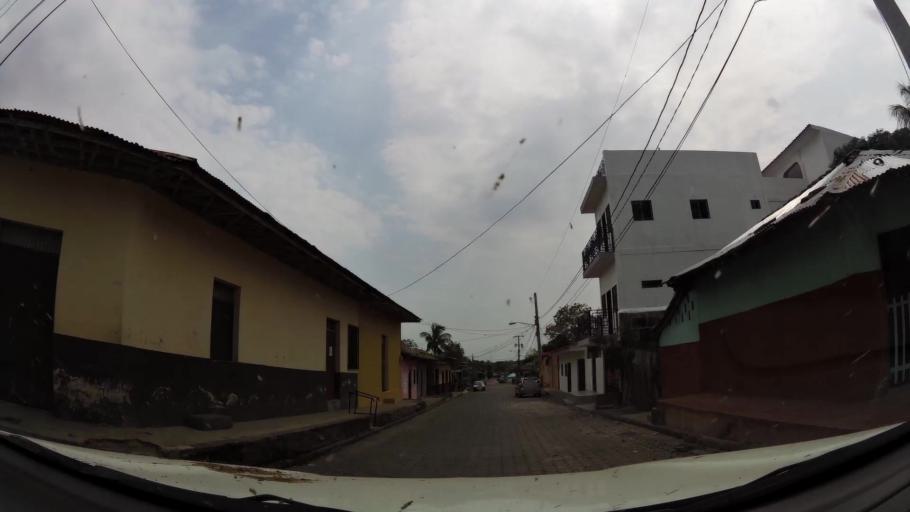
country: NI
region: Granada
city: Diria
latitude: 11.8865
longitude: -86.0546
